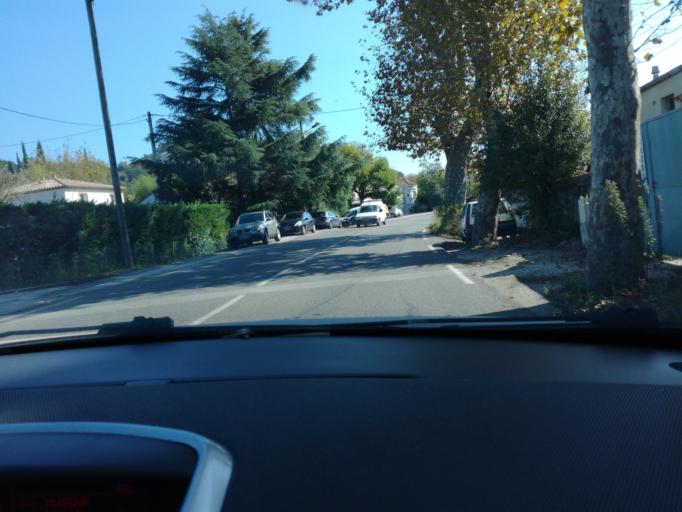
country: FR
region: Provence-Alpes-Cote d'Azur
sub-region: Departement du Var
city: Hyeres
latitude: 43.1255
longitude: 6.1130
